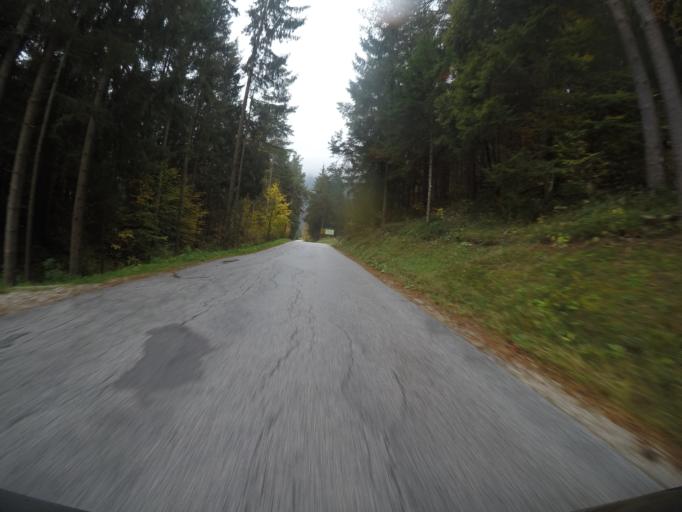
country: SI
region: Kranjska Gora
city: Mojstrana
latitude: 46.4549
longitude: 13.9317
